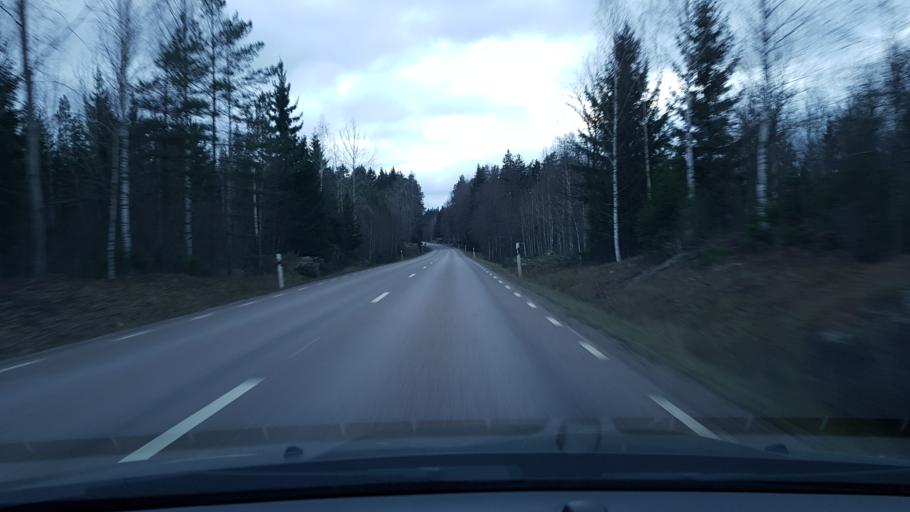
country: SE
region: Uppsala
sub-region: Osthammars Kommun
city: Gimo
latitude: 59.9670
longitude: 18.1150
